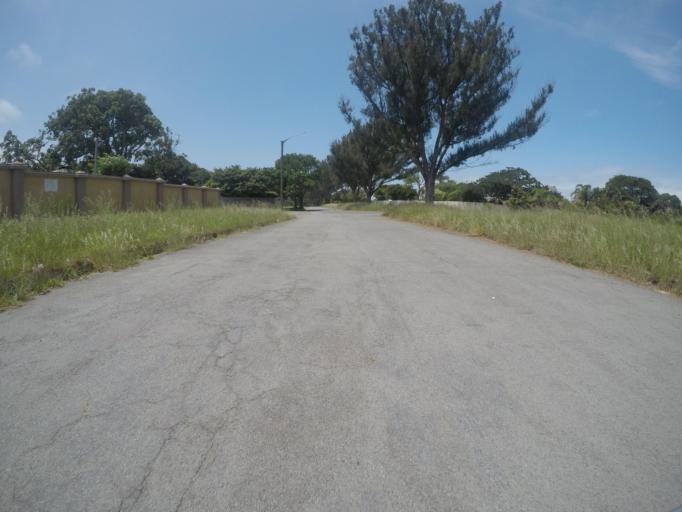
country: ZA
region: Eastern Cape
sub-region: Buffalo City Metropolitan Municipality
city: East London
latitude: -32.9978
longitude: 27.9280
